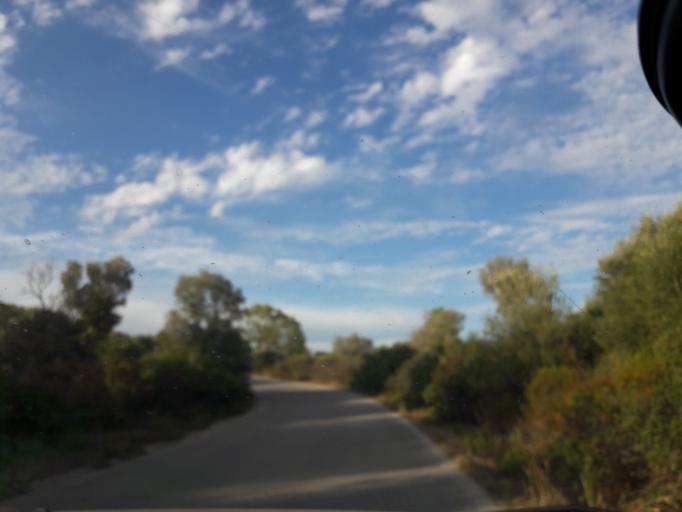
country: GR
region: Central Macedonia
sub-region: Nomos Chalkidikis
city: Nea Roda
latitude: 40.3325
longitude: 23.8985
